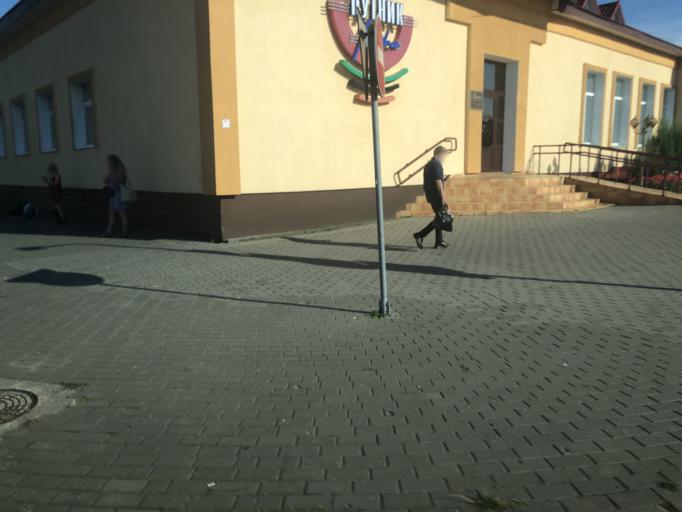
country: BY
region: Grodnenskaya
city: Hrodna
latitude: 53.6778
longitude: 23.8426
